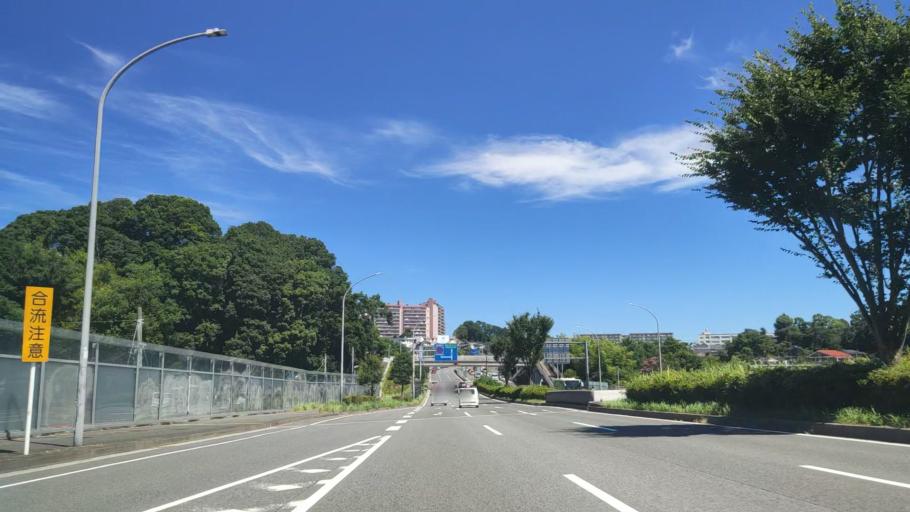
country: JP
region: Kanagawa
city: Yokohama
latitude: 35.4456
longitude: 139.5601
